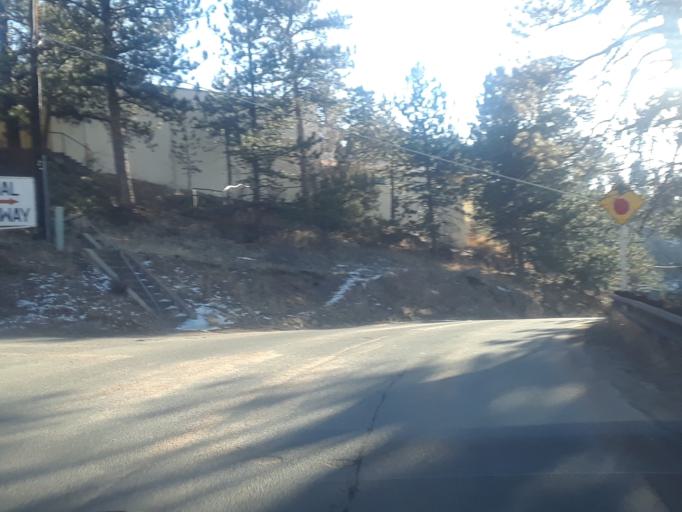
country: US
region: Colorado
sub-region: Larimer County
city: Estes Park
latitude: 40.3720
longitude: -105.5223
